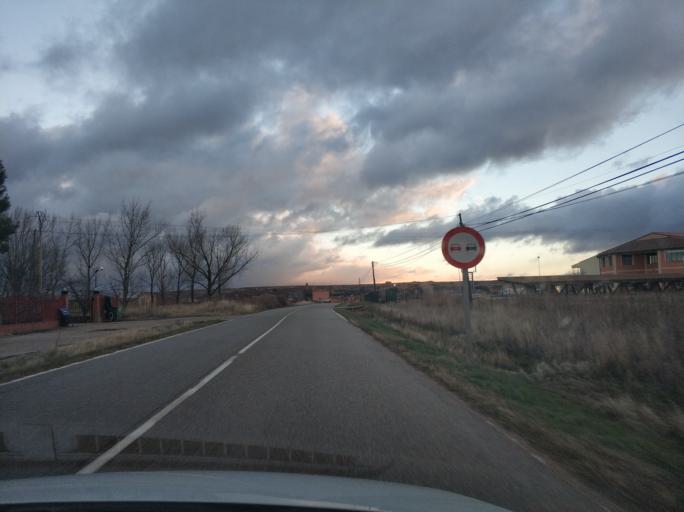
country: ES
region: Castille and Leon
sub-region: Provincia de Segovia
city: Ayllon
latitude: 41.4160
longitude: -3.3900
